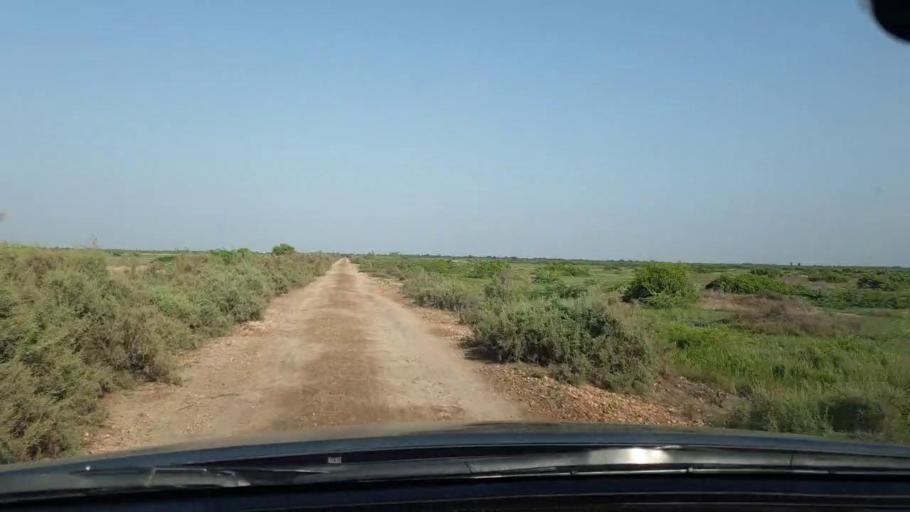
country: PK
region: Sindh
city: Naukot
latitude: 24.8337
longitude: 69.2419
